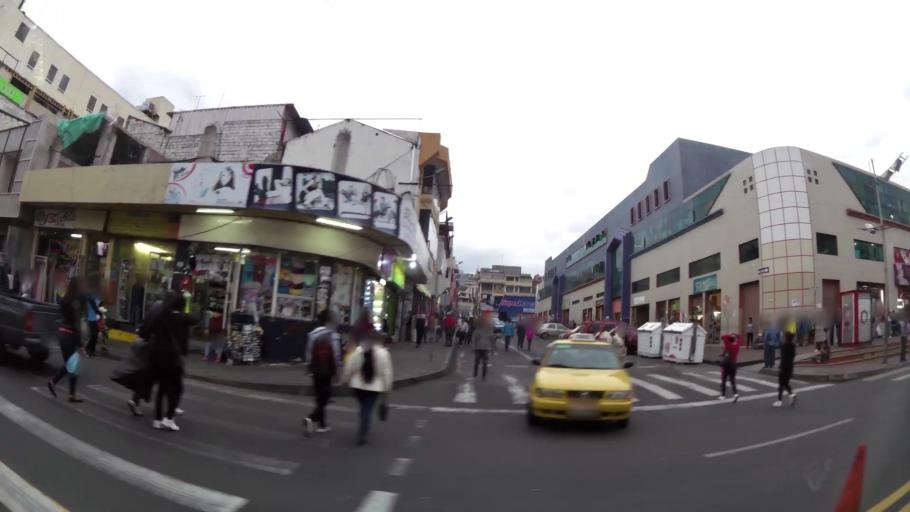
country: EC
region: Tungurahua
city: Ambato
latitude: -1.2400
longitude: -78.6251
